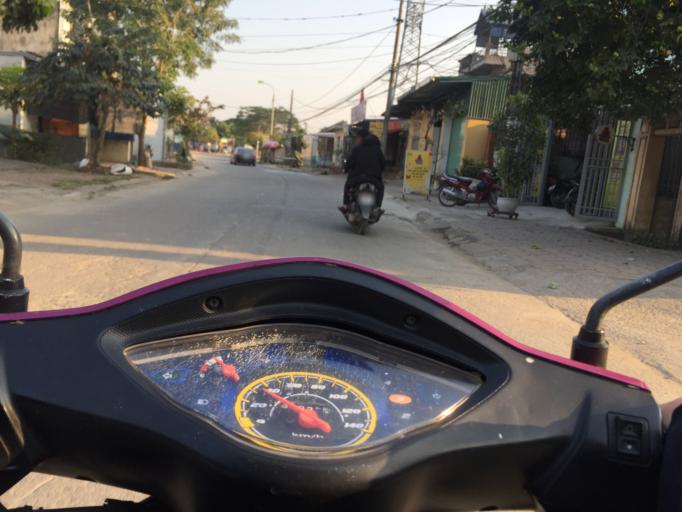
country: VN
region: Ha Noi
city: Chuc Son
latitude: 20.9192
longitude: 105.7133
